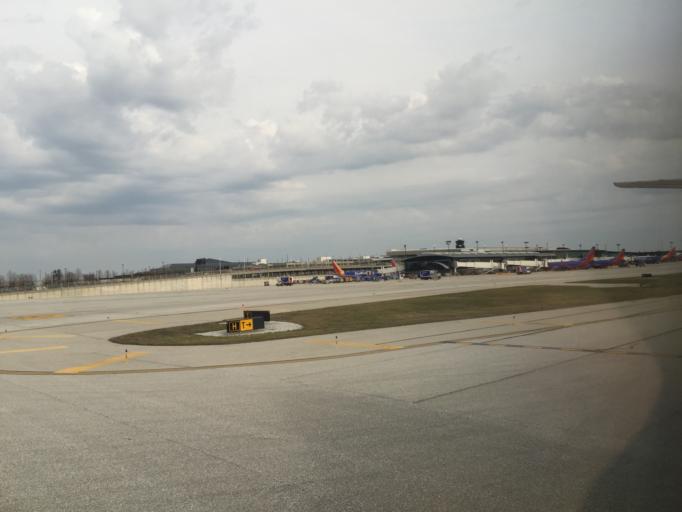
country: US
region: Maryland
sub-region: Anne Arundel County
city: Linthicum
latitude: 39.1815
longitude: -76.6768
